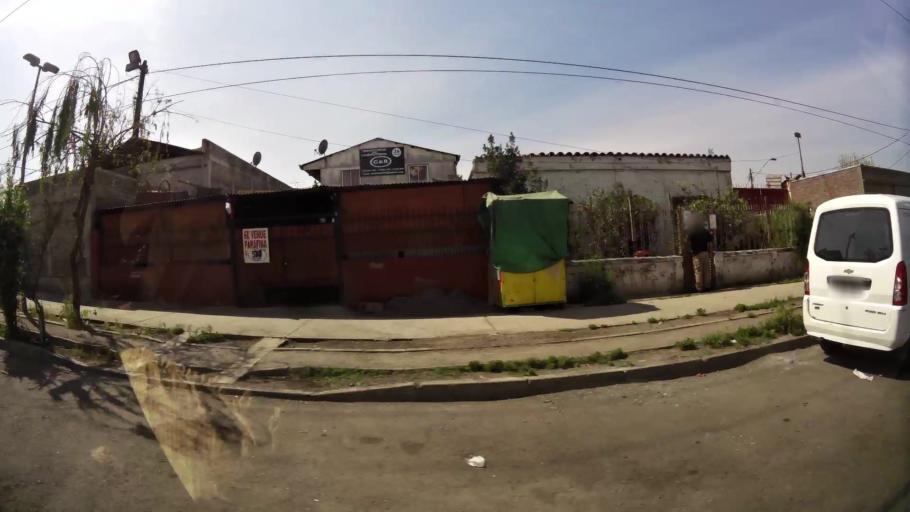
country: CL
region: Santiago Metropolitan
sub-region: Provincia de Santiago
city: Lo Prado
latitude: -33.4433
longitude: -70.7309
